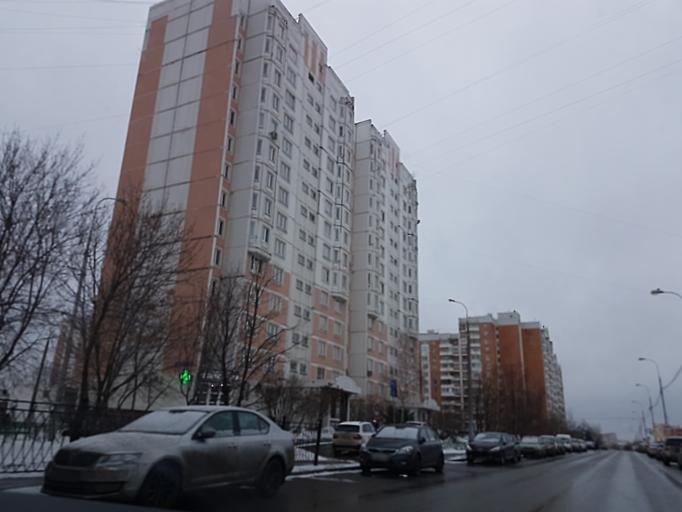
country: RU
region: Moskovskaya
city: Pavshino
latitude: 55.8316
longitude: 37.3535
